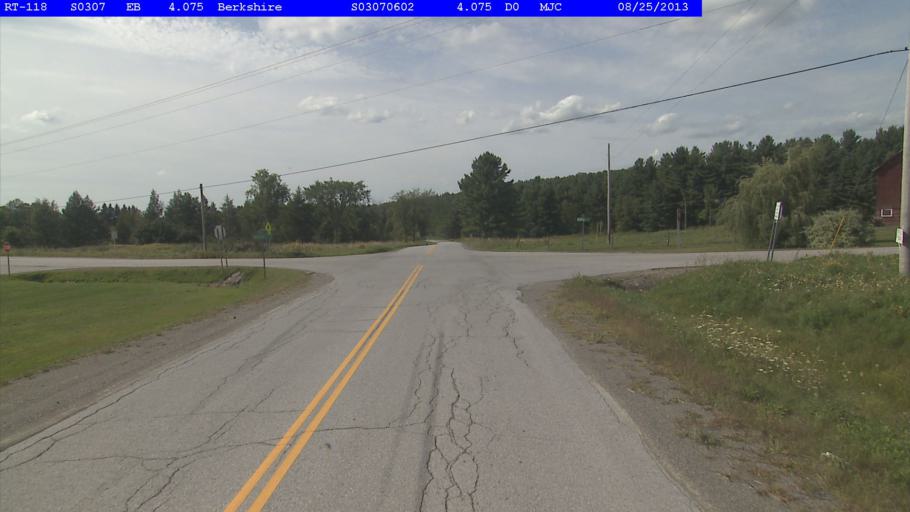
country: US
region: Vermont
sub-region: Franklin County
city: Enosburg Falls
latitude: 44.9730
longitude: -72.7658
